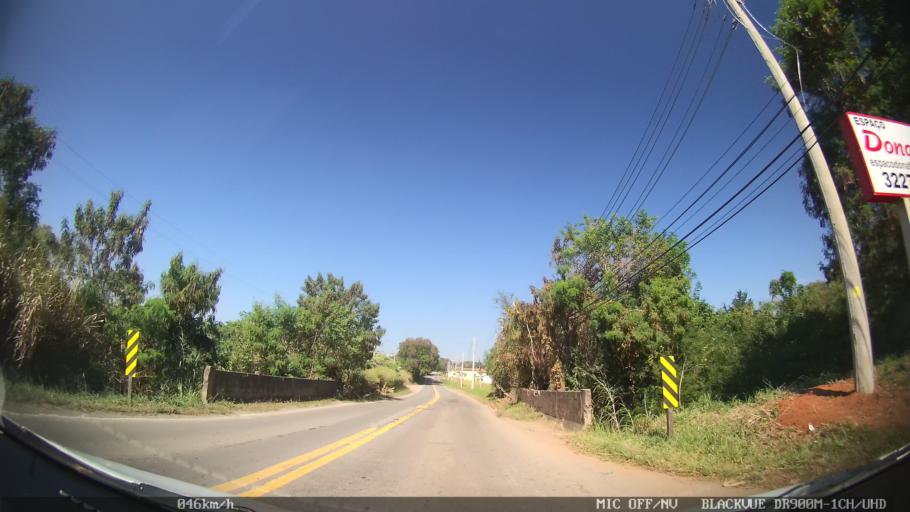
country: BR
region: Sao Paulo
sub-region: Campinas
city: Campinas
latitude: -22.9920
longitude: -47.0860
